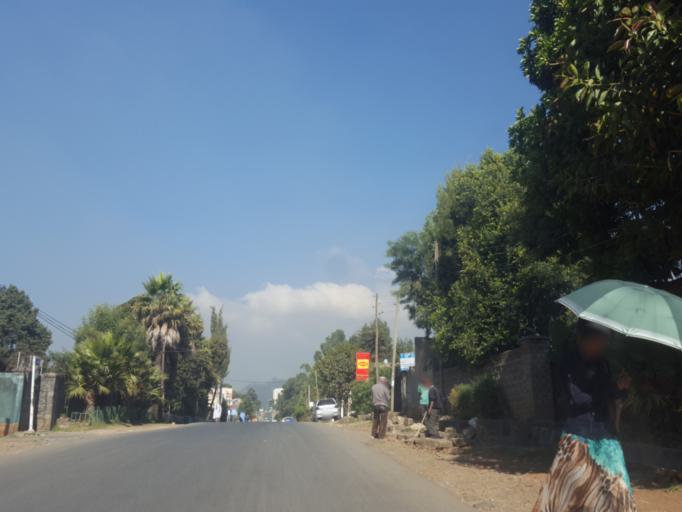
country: ET
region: Adis Abeba
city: Addis Ababa
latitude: 9.0535
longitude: 38.7307
